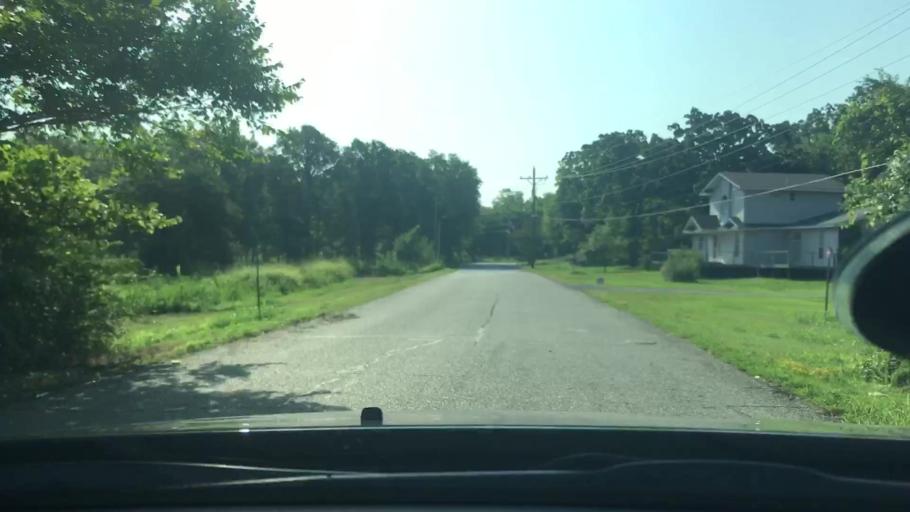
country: US
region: Oklahoma
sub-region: Atoka County
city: Atoka
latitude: 34.3899
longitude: -96.1316
